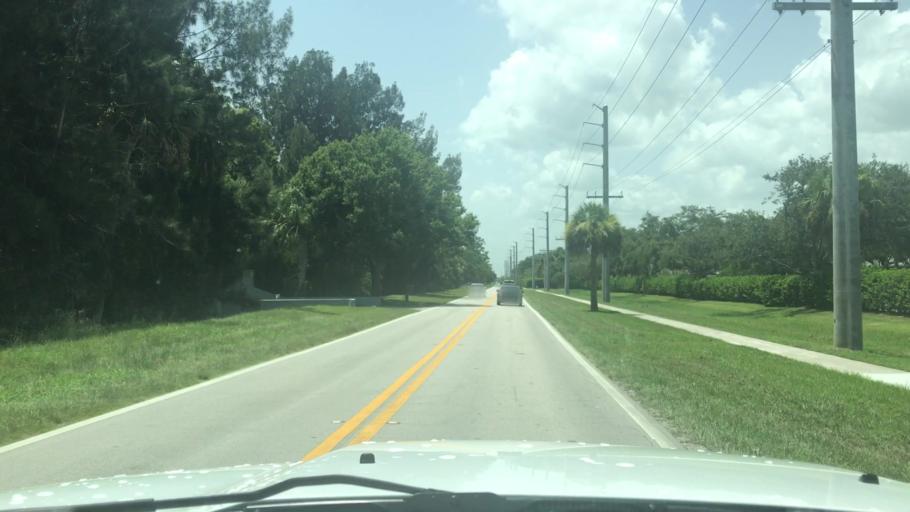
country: US
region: Florida
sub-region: Indian River County
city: Vero Beach South
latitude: 27.6239
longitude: -80.4320
